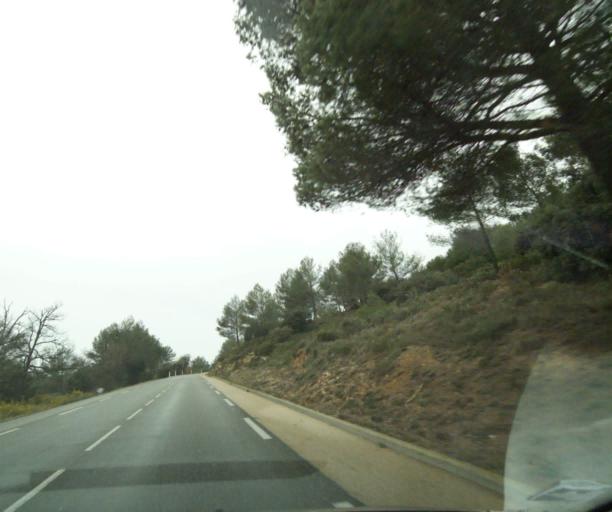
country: FR
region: Provence-Alpes-Cote d'Azur
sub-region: Departement des Bouches-du-Rhone
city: Rognes
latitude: 43.6607
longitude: 5.3817
